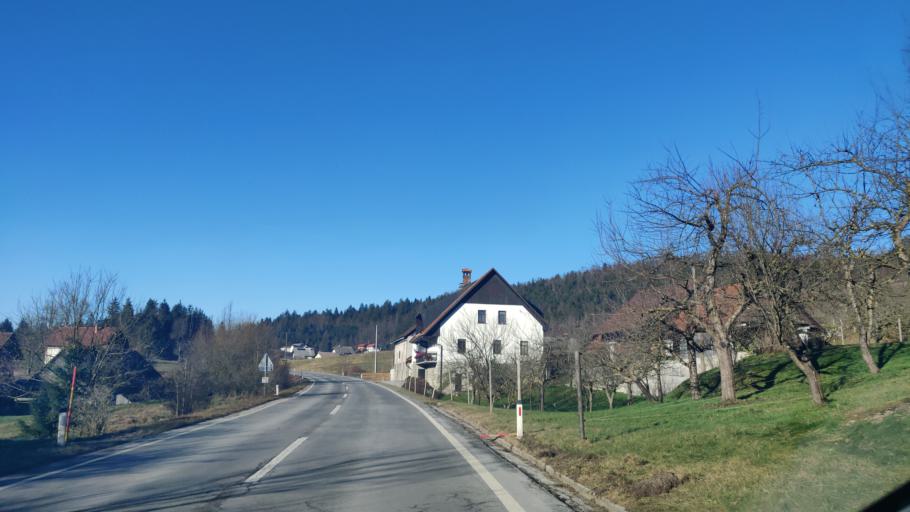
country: SI
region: Logatec
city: Logatec
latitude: 45.8740
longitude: 14.2128
